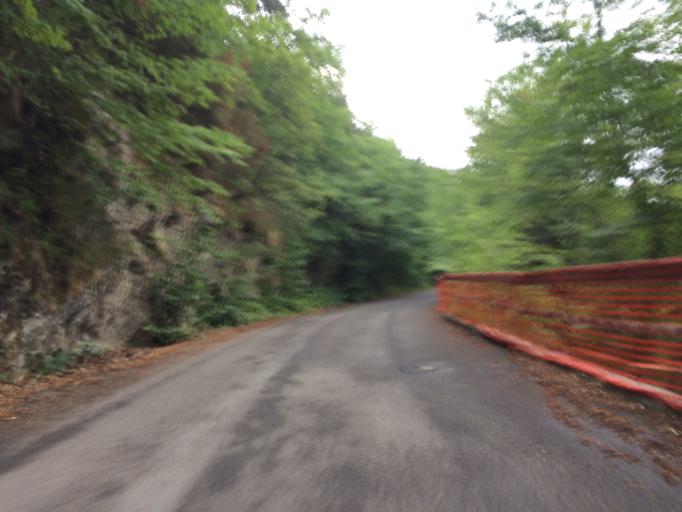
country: IT
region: Liguria
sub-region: Provincia di Imperia
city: Triora
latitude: 43.9814
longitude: 7.7481
